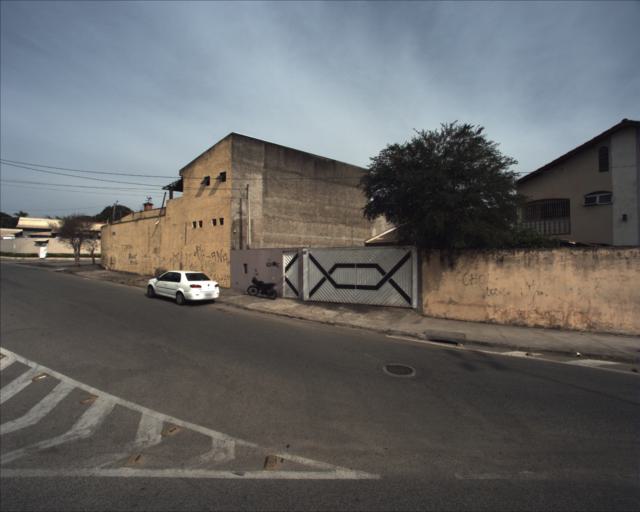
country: BR
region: Sao Paulo
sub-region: Sorocaba
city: Sorocaba
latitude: -23.4755
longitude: -47.4556
